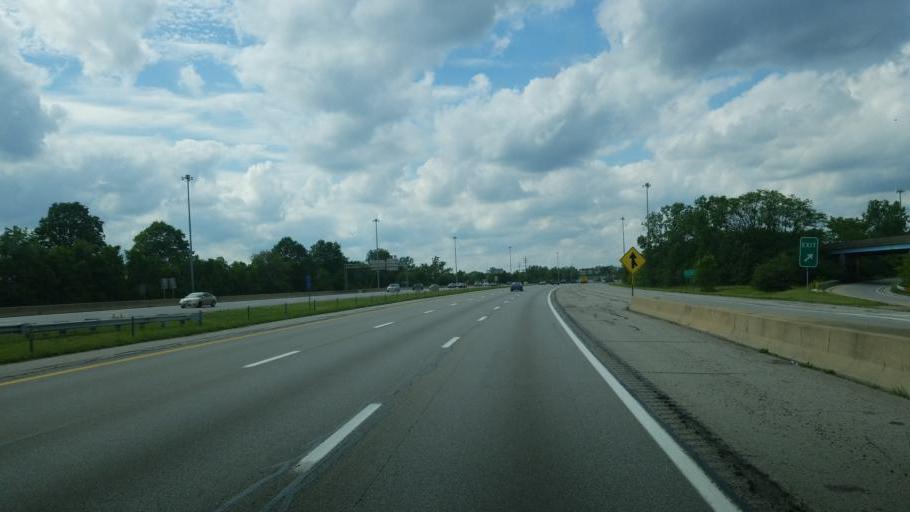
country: US
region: Ohio
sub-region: Franklin County
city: Whitehall
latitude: 39.9797
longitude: -82.8537
